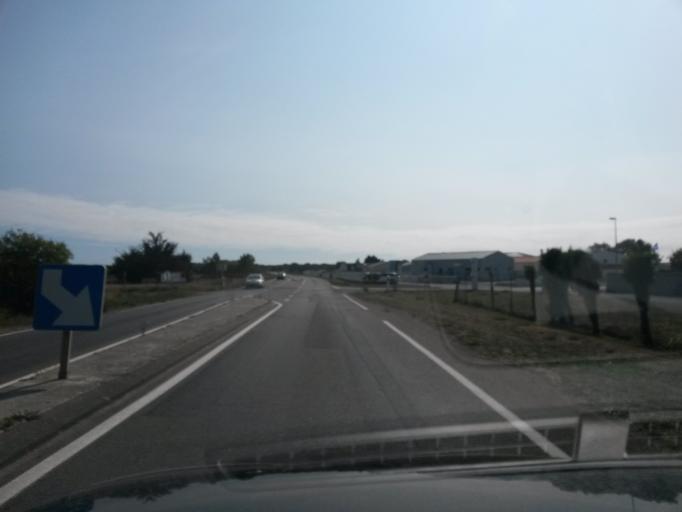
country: FR
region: Pays de la Loire
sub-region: Departement de la Vendee
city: Bretignolles-sur-Mer
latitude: 46.5982
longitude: -1.8243
